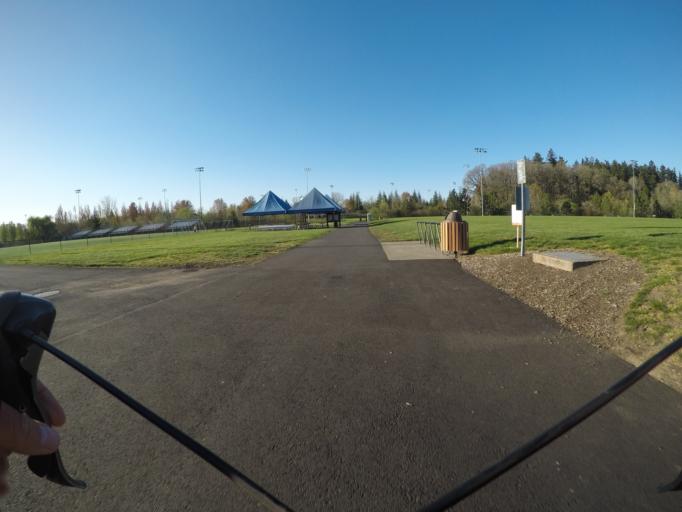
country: US
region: Oregon
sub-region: Washington County
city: Oak Hills
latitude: 45.5205
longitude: -122.8356
